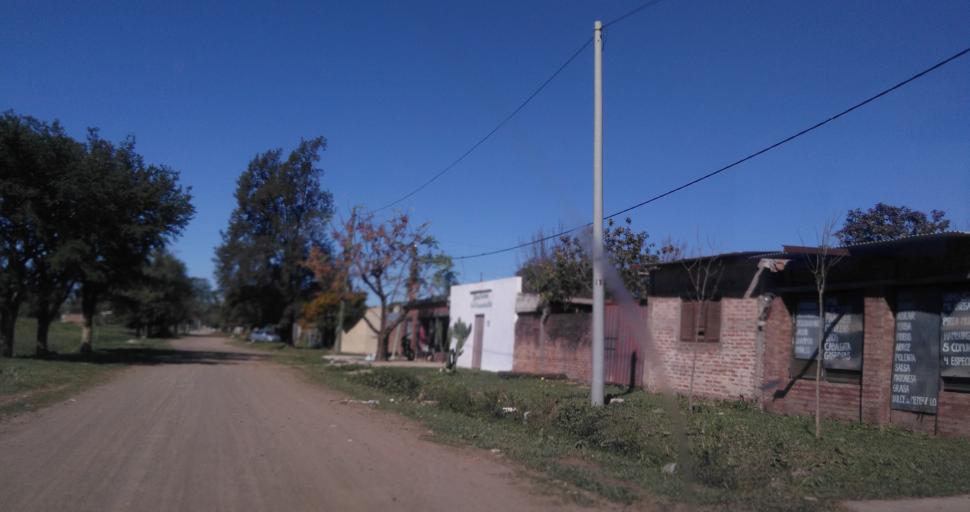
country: AR
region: Chaco
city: Fontana
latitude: -27.4304
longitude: -59.0191
